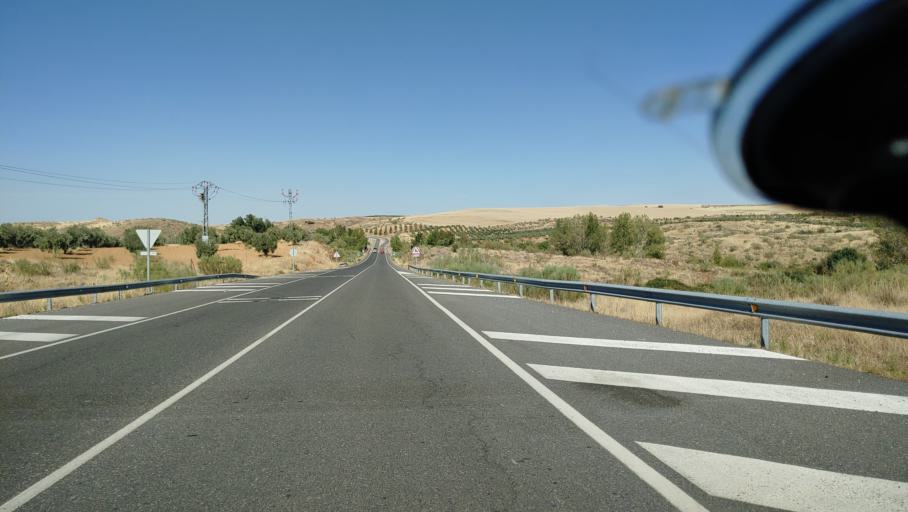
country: ES
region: Castille-La Mancha
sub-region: Province of Toledo
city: Casasbuenas
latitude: 39.7414
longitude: -4.0952
